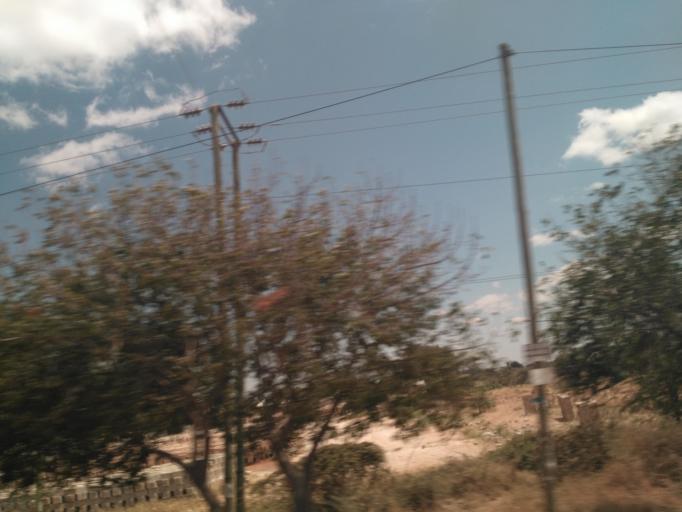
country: TZ
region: Dodoma
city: Kisasa
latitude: -6.1695
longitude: 35.7756
